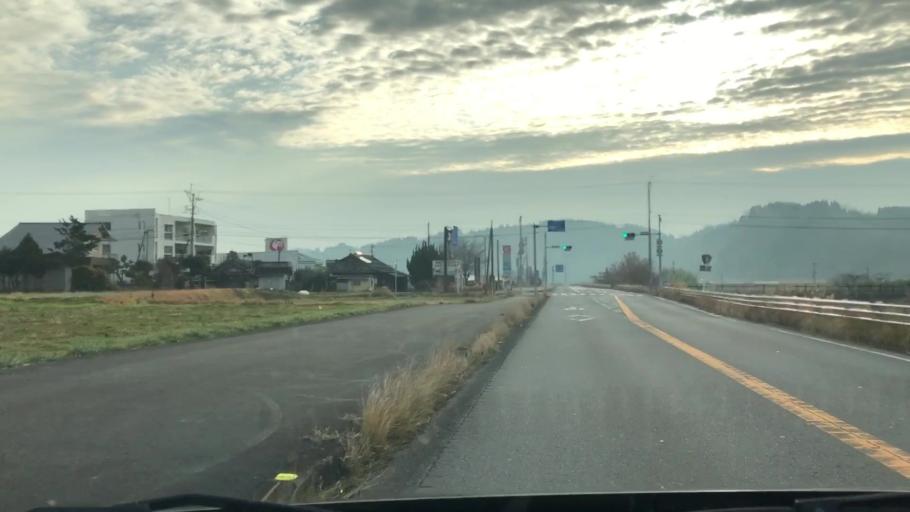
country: JP
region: Oita
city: Takedamachi
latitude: 32.9666
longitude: 131.4803
